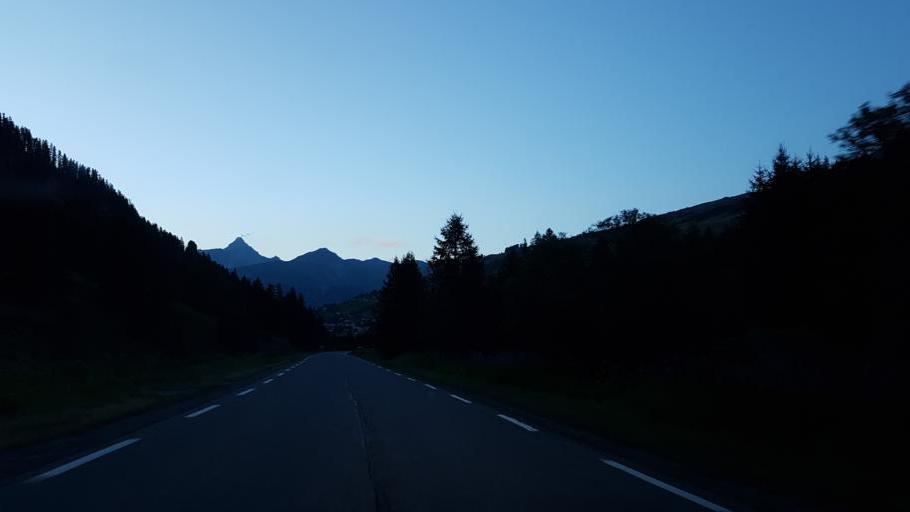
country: IT
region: Piedmont
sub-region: Provincia di Cuneo
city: Pontechianale
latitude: 44.7141
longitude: 6.8484
